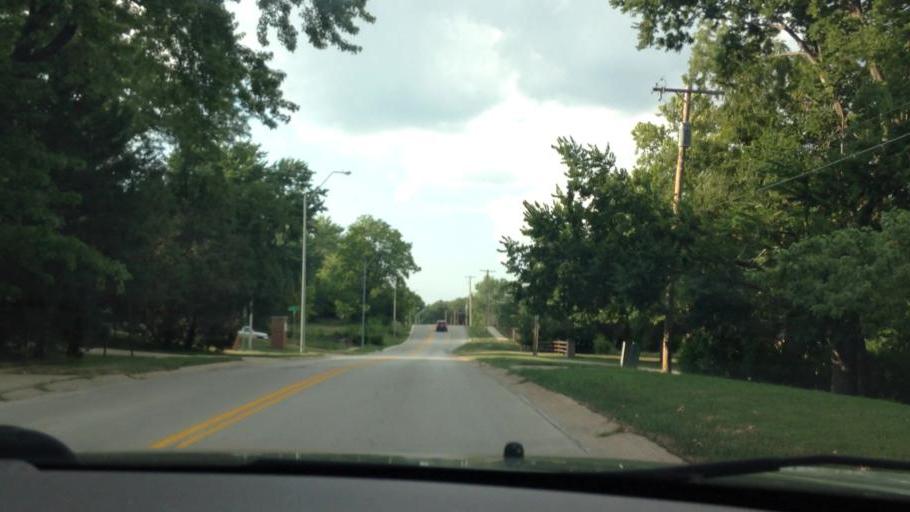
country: US
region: Missouri
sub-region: Platte County
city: Parkville
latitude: 39.2208
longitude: -94.6404
